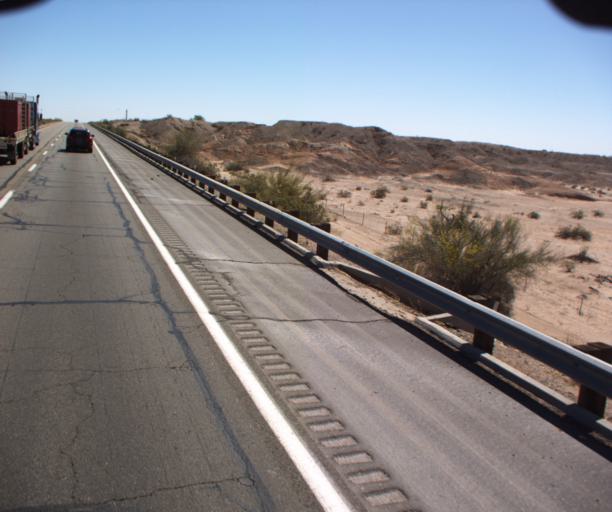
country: US
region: Arizona
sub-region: Yuma County
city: Wellton
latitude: 32.6624
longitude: -114.2655
